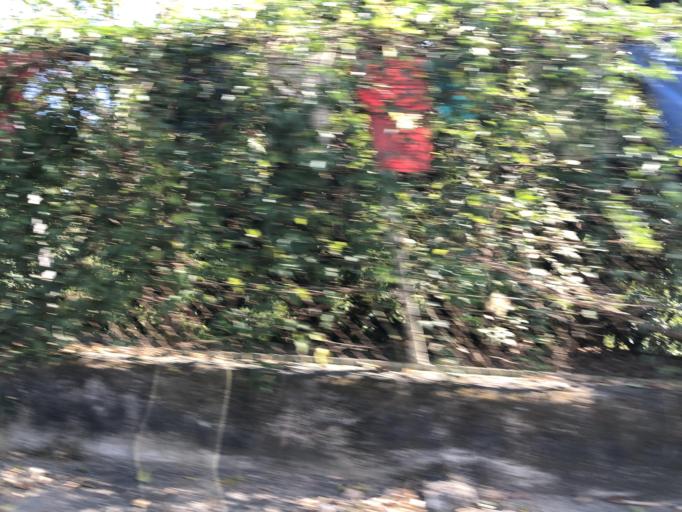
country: TW
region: Taiwan
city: Yujing
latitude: 23.0516
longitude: 120.3807
